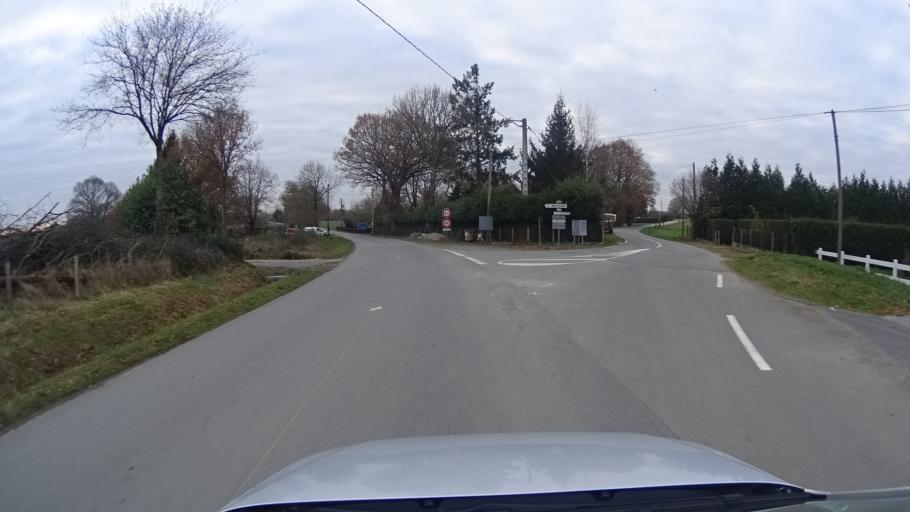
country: FR
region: Brittany
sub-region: Departement d'Ille-et-Vilaine
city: Sainte-Marie
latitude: 47.6928
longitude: -1.9342
